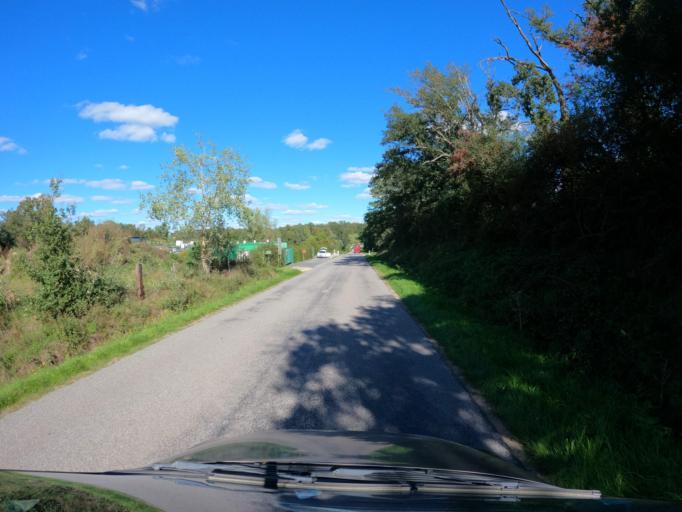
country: FR
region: Auvergne
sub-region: Departement de l'Allier
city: Doyet
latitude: 46.3965
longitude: 2.8678
